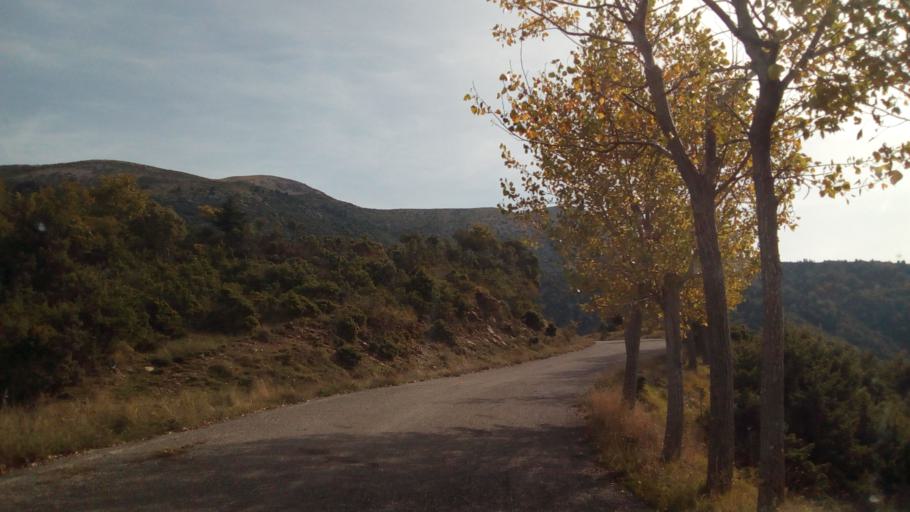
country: GR
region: West Greece
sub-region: Nomos Aitolias kai Akarnanias
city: Thermo
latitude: 38.5571
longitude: 21.8123
